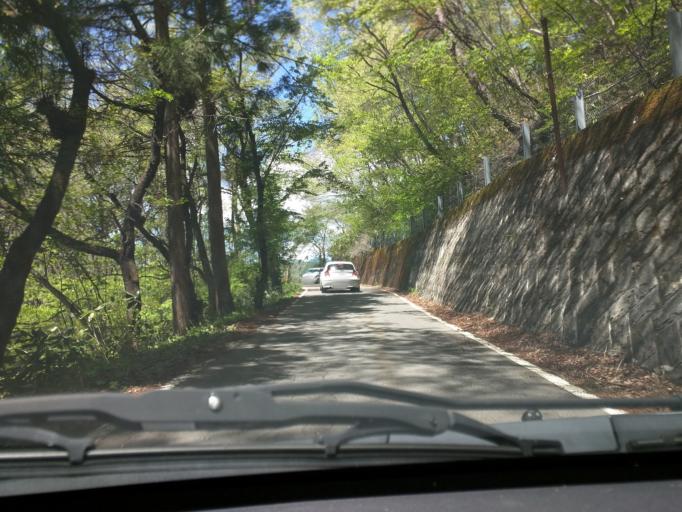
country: JP
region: Nagano
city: Nagano-shi
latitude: 36.6751
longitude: 138.1121
